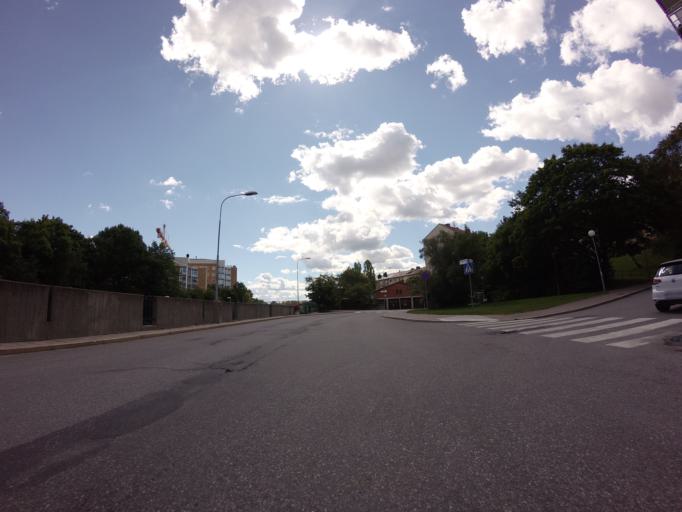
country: SE
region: Stockholm
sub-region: Stockholms Kommun
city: Stockholm
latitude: 59.3506
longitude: 18.0647
